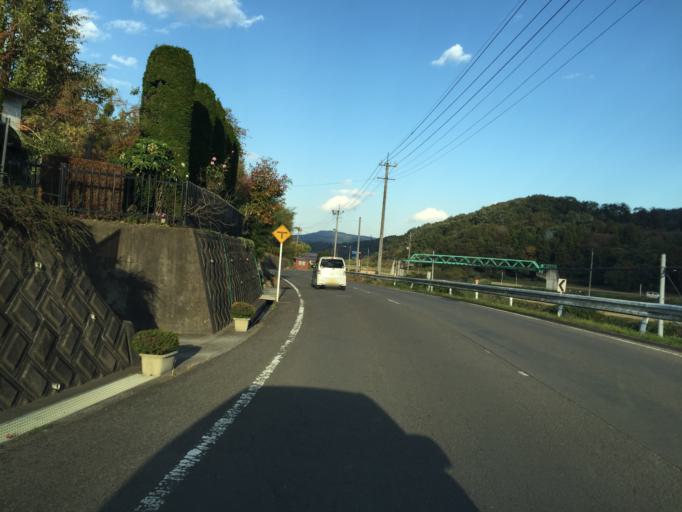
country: JP
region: Fukushima
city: Fukushima-shi
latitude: 37.7018
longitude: 140.4228
